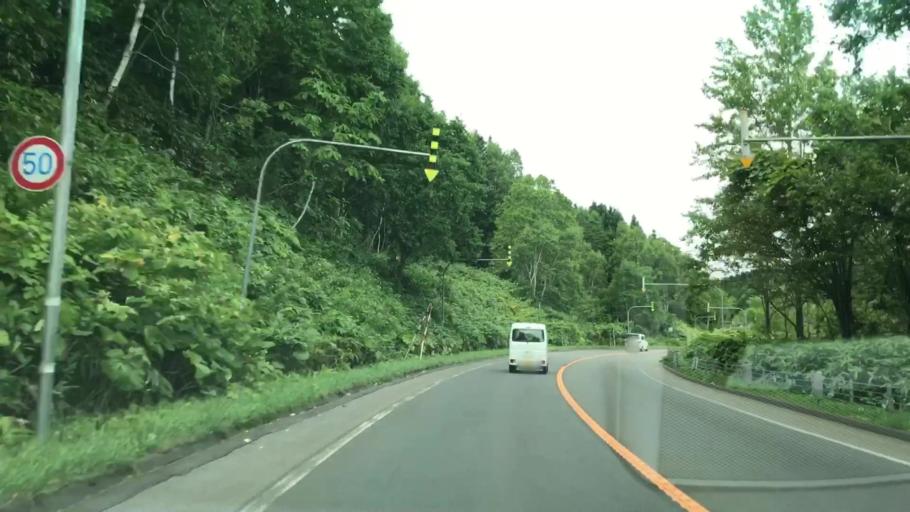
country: JP
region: Hokkaido
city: Niseko Town
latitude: 42.9281
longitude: 140.7152
